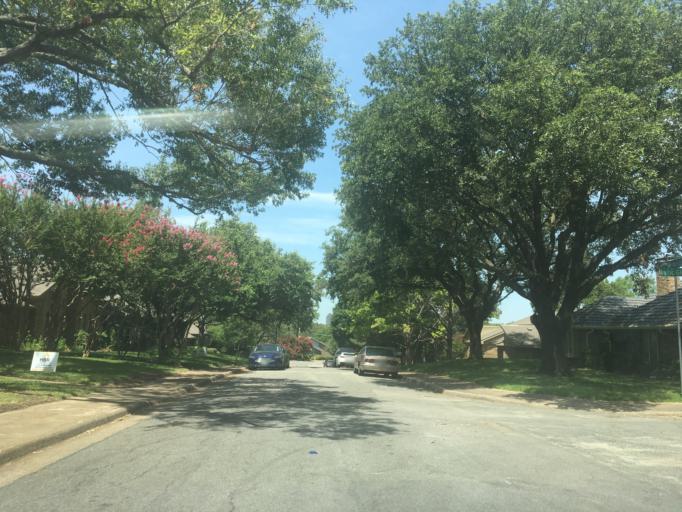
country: US
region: Texas
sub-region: Dallas County
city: Richardson
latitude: 32.8830
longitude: -96.7383
